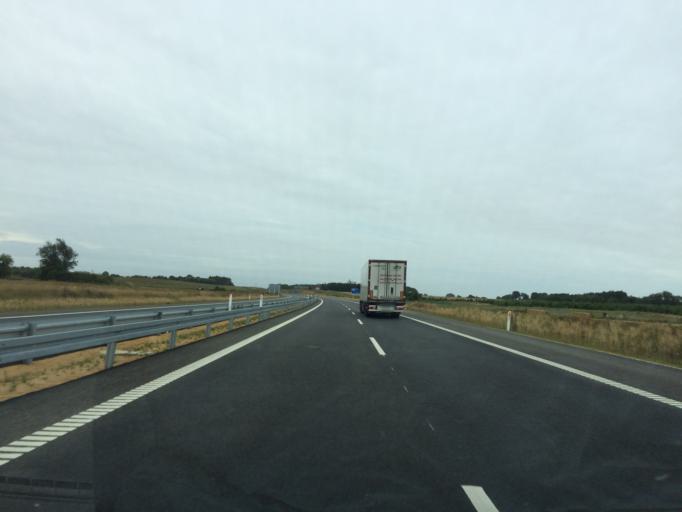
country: DK
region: Central Jutland
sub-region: Herning Kommune
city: Snejbjerg
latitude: 56.1430
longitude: 8.8694
